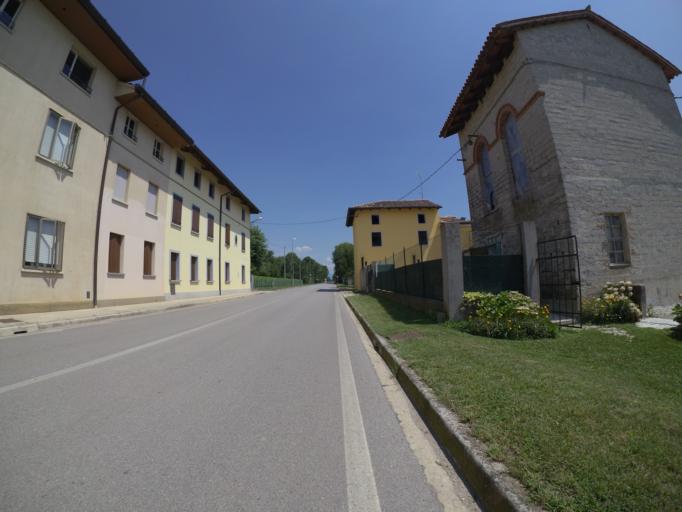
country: IT
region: Friuli Venezia Giulia
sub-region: Provincia di Udine
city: Basiliano-Vissandone
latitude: 45.9839
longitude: 13.0963
